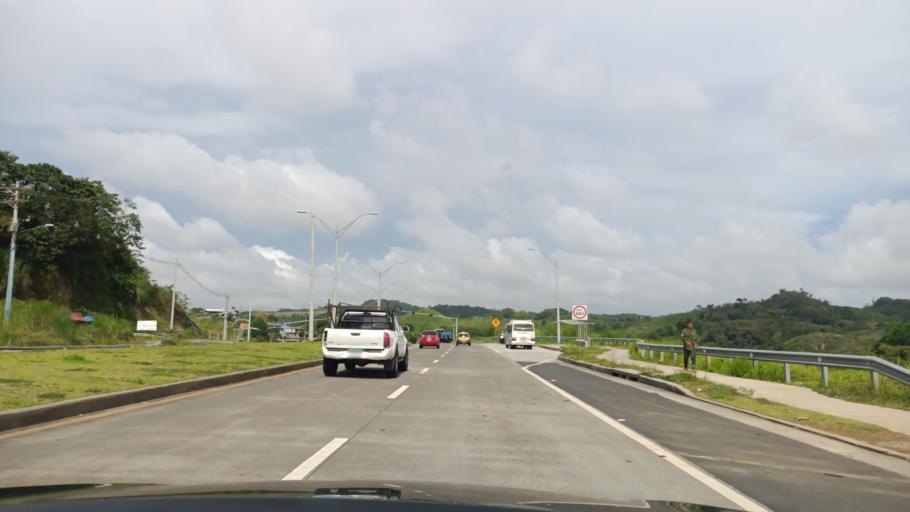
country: PA
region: Panama
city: Las Cumbres
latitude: 9.0982
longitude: -79.4878
